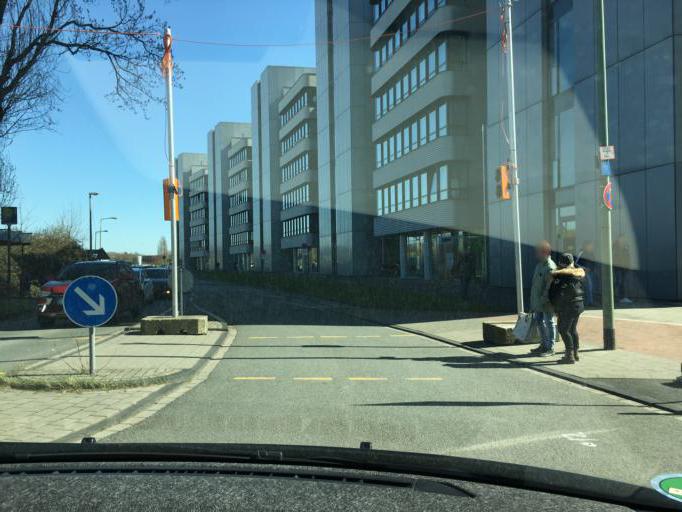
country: DE
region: North Rhine-Westphalia
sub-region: Regierungsbezirk Dusseldorf
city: Duisburg
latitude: 51.4395
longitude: 6.7628
